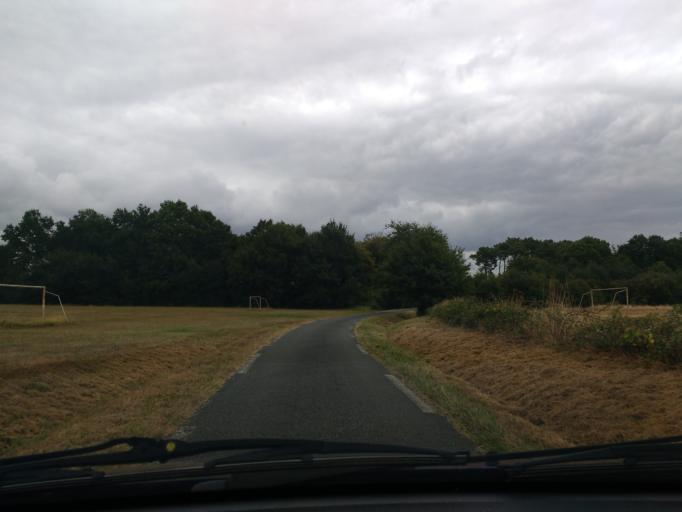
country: FR
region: Aquitaine
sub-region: Departement de la Gironde
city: Gradignan
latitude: 44.7785
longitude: -0.6256
